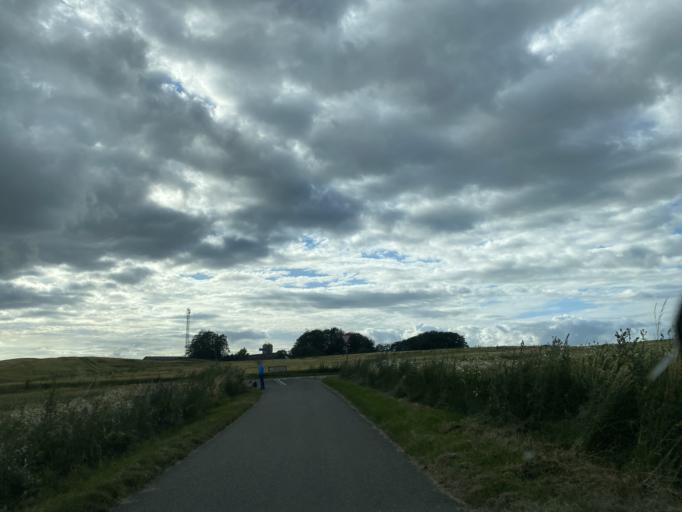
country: DK
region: Central Jutland
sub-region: Syddjurs Kommune
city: Ronde
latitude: 56.2888
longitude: 10.5734
